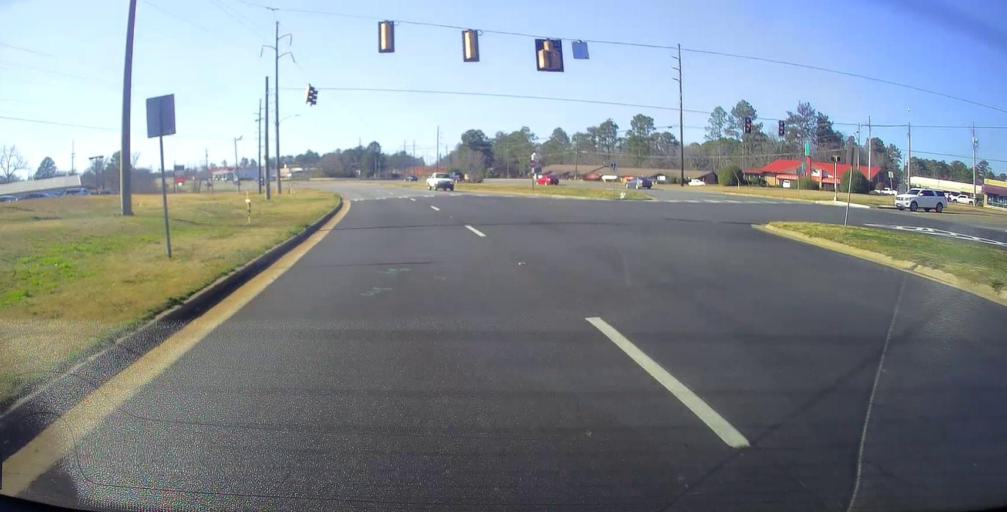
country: US
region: Georgia
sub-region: Sumter County
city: Americus
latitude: 32.0705
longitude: -84.2079
